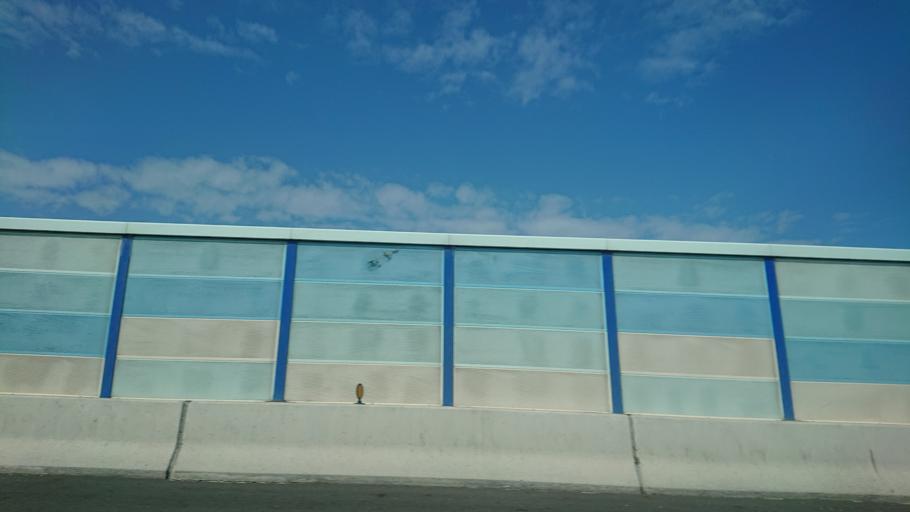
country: TW
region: Taiwan
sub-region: Changhua
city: Chang-hua
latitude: 23.9507
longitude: 120.3288
